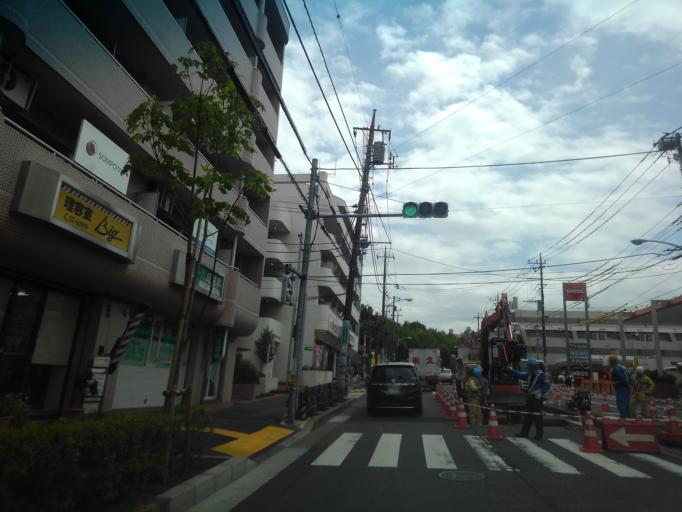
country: JP
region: Tokyo
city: Hino
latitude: 35.6333
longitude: 139.4474
